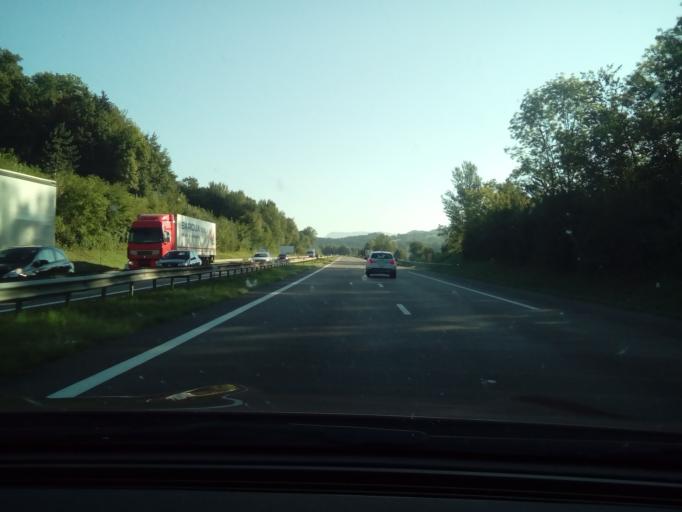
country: FR
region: Rhone-Alpes
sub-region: Departement de la Haute-Savoie
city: Viuz-la-Chiesaz
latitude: 45.8302
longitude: 6.0422
